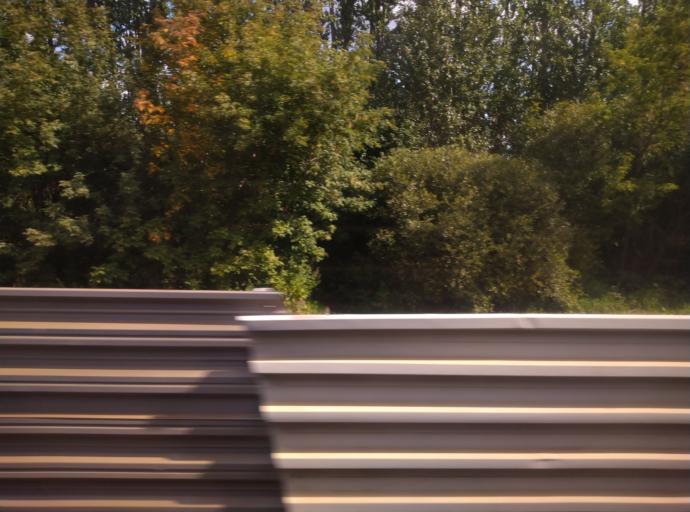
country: RU
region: St.-Petersburg
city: Kupchino
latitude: 59.8803
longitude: 30.4063
